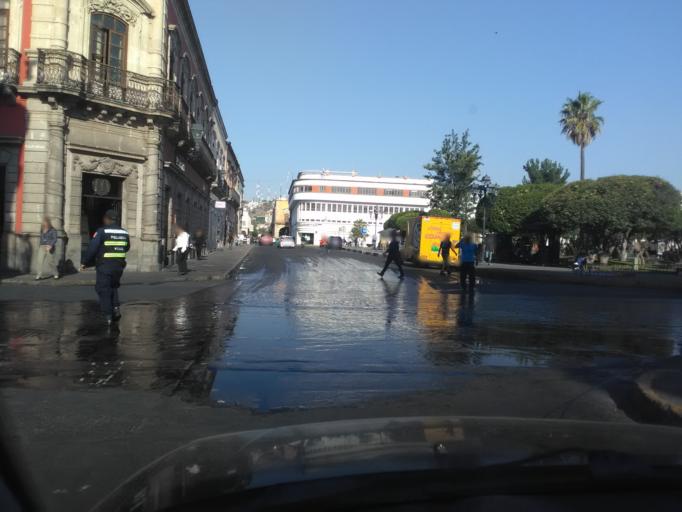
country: MX
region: Durango
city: Victoria de Durango
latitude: 24.0234
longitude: -104.6696
